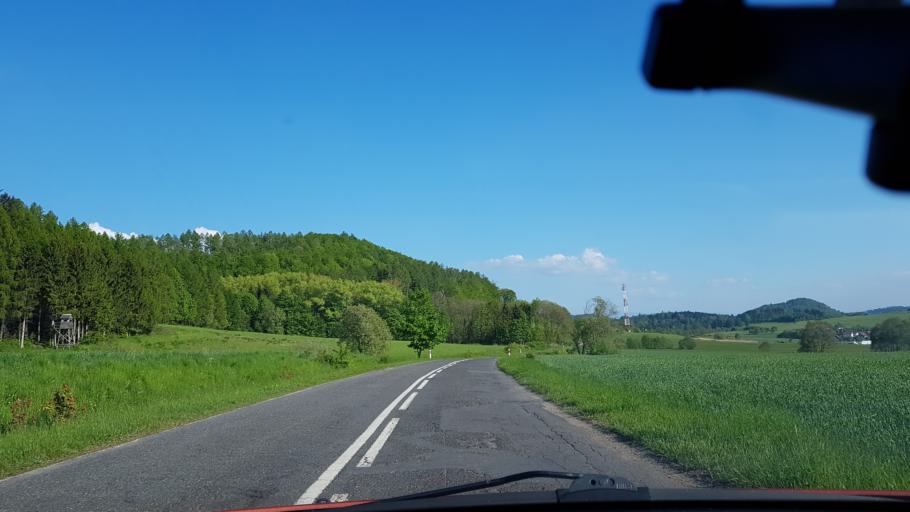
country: PL
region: Lower Silesian Voivodeship
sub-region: Powiat klodzki
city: Bozkow
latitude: 50.5866
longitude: 16.5822
